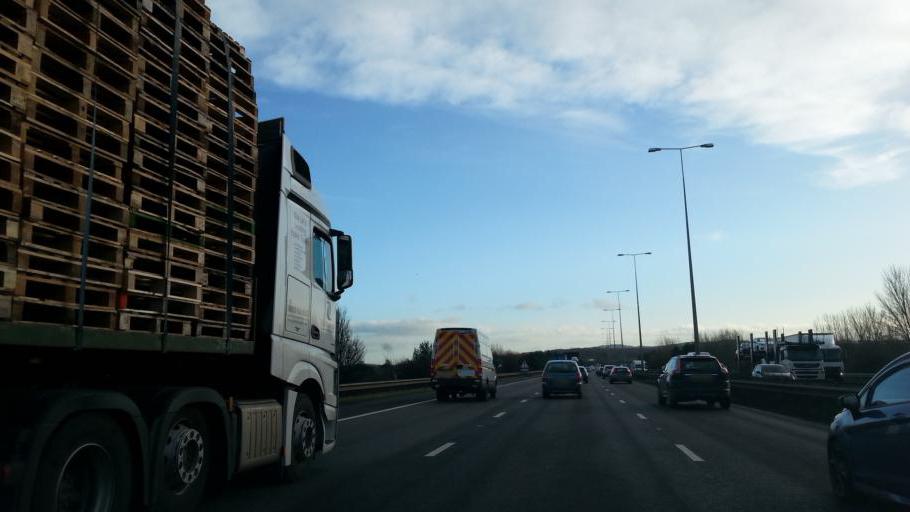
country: GB
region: England
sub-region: Leicestershire
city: Shepshed
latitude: 52.7848
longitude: -1.2842
